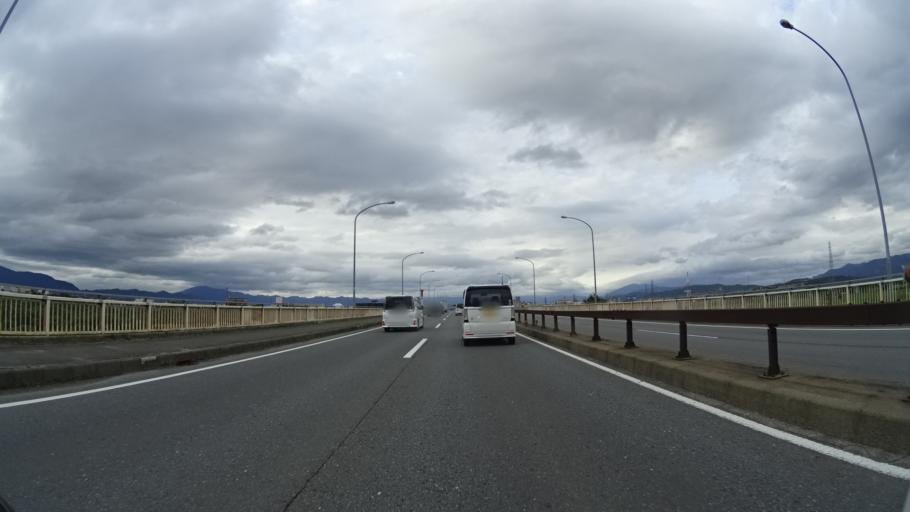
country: JP
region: Kyoto
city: Yawata
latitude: 34.9155
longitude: 135.7446
